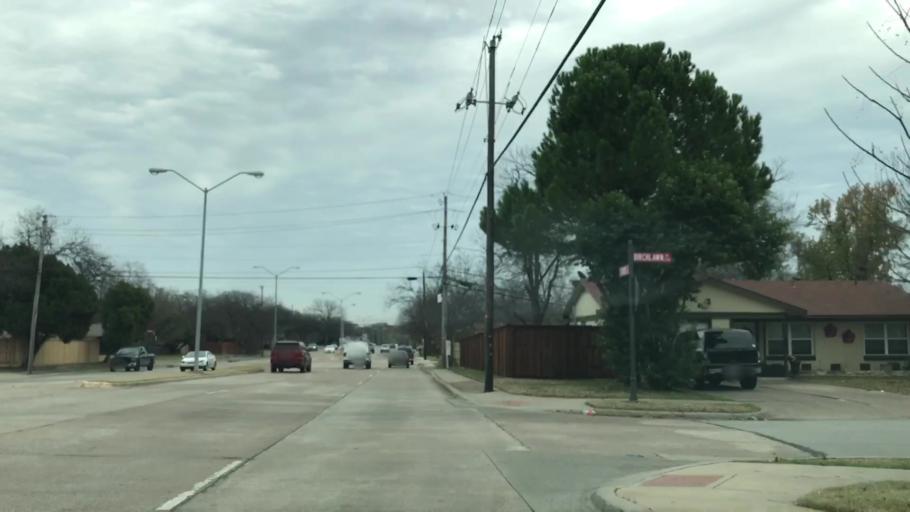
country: US
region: Texas
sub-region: Dallas County
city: Farmers Branch
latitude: 32.9320
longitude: -96.8860
